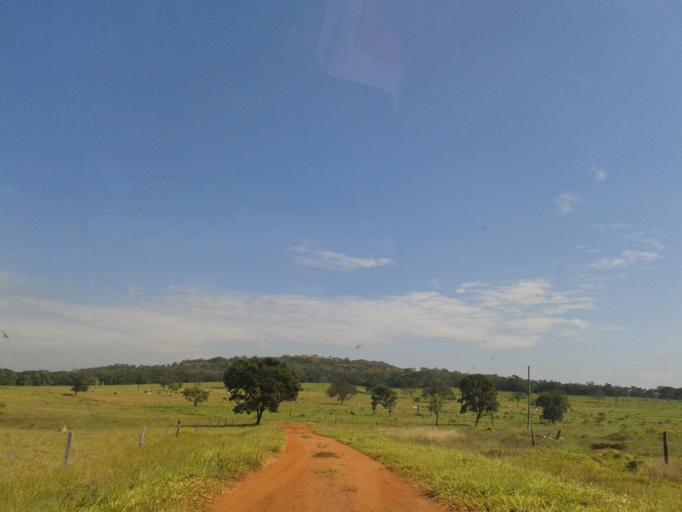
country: BR
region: Minas Gerais
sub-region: Campina Verde
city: Campina Verde
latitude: -19.3908
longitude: -49.6309
